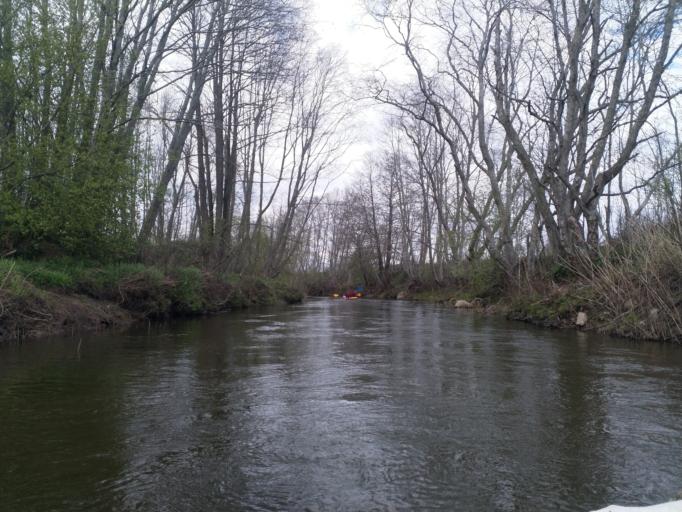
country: LV
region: Alsunga
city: Alsunga
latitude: 57.1206
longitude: 21.5475
